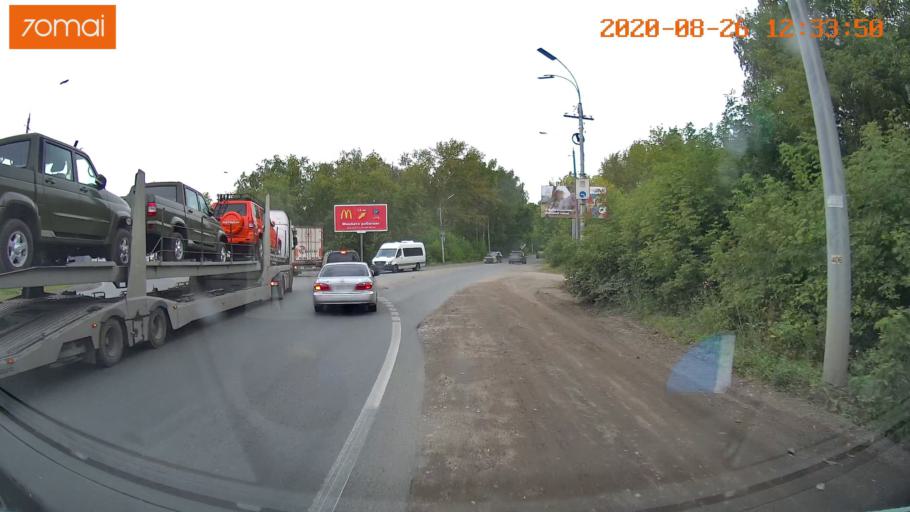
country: RU
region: Rjazan
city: Ryazan'
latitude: 54.5837
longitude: 39.7738
